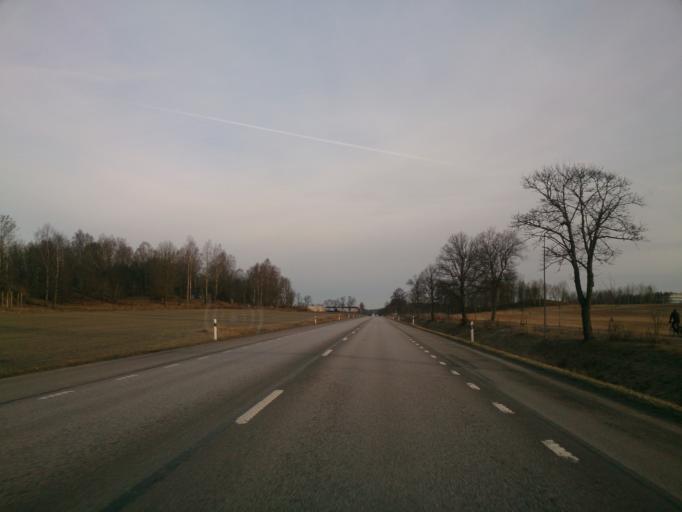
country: SE
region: OEstergoetland
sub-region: Atvidabergs Kommun
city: Atvidaberg
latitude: 58.2215
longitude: 15.9715
